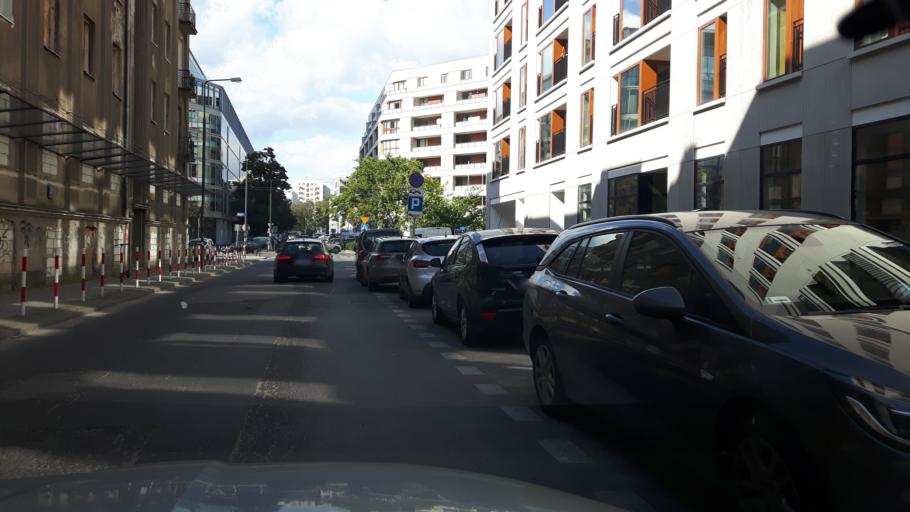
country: PL
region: Masovian Voivodeship
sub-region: Warszawa
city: Wola
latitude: 52.2355
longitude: 20.9847
